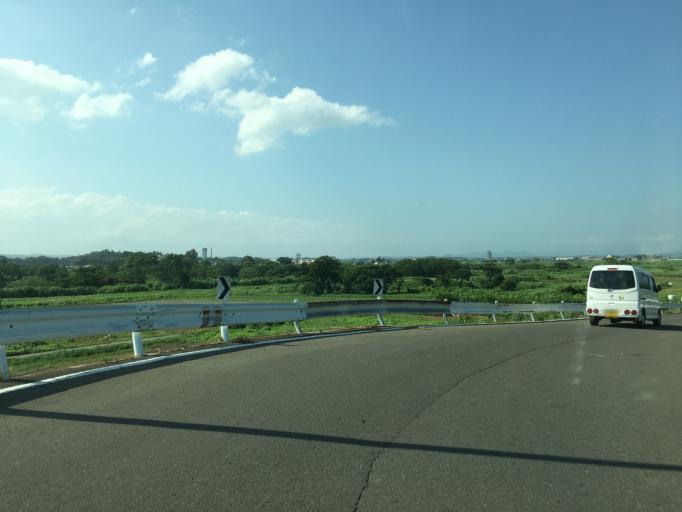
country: JP
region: Miyagi
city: Kakuda
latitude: 37.9601
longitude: 140.7896
